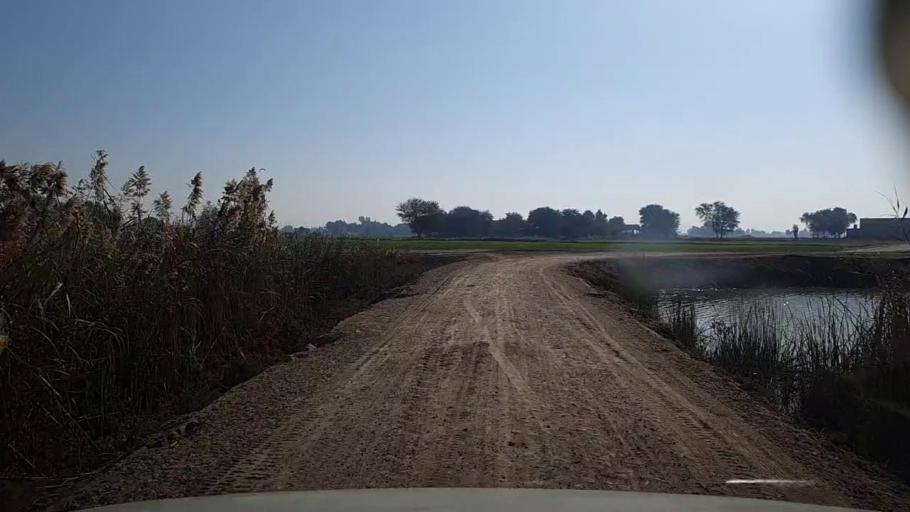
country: PK
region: Sindh
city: Khairpur
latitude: 28.0540
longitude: 69.7418
